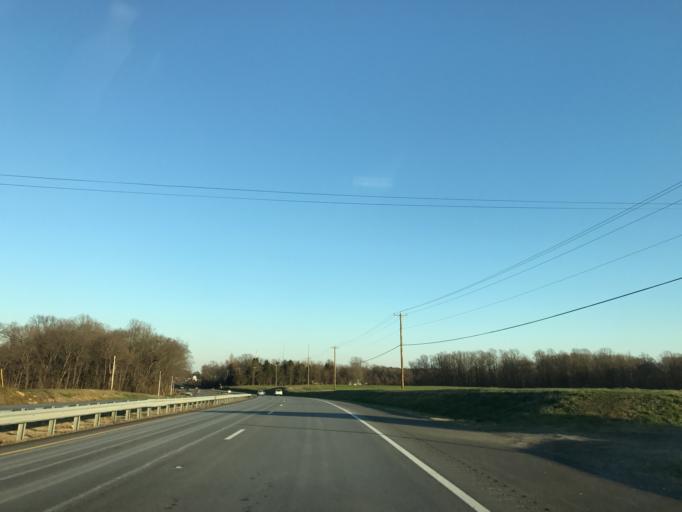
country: US
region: Maryland
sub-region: Queen Anne's County
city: Centreville
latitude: 38.9672
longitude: -76.1162
